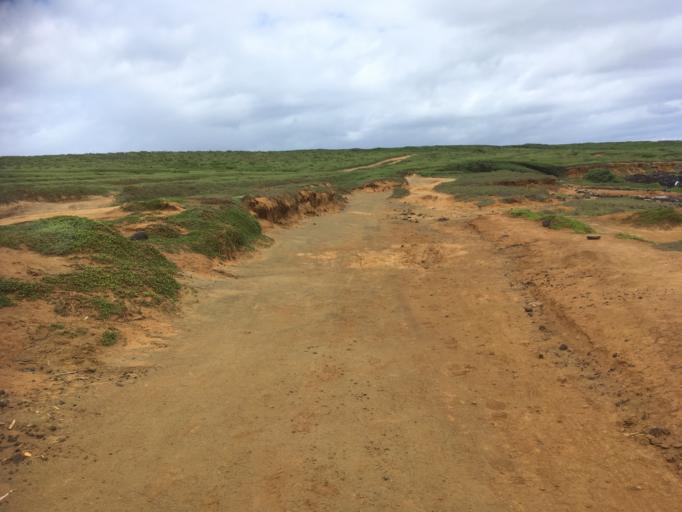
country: US
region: Hawaii
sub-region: Hawaii County
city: Hawaiian Ocean View
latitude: 18.9194
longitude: -155.6644
